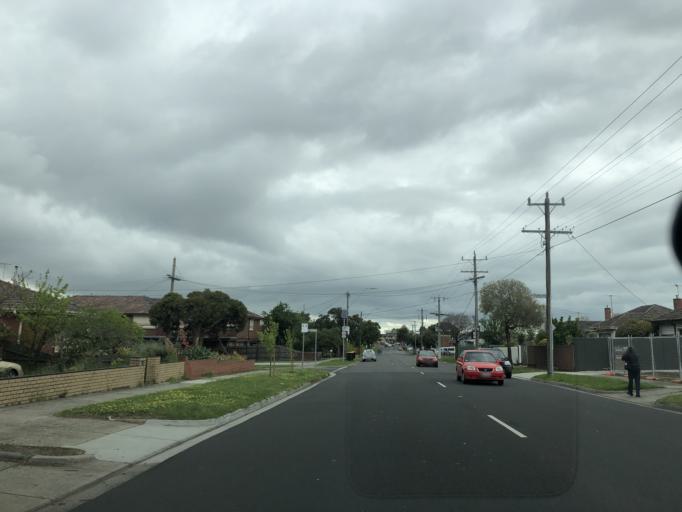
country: AU
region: Victoria
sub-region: Greater Dandenong
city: Dandenong North
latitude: -37.9716
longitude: 145.2046
